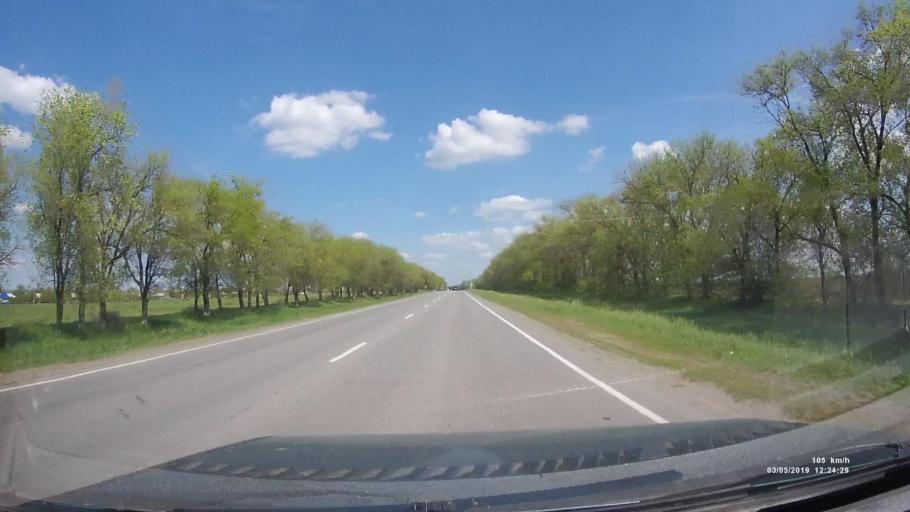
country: RU
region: Rostov
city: Semikarakorsk
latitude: 47.4207
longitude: 40.6999
